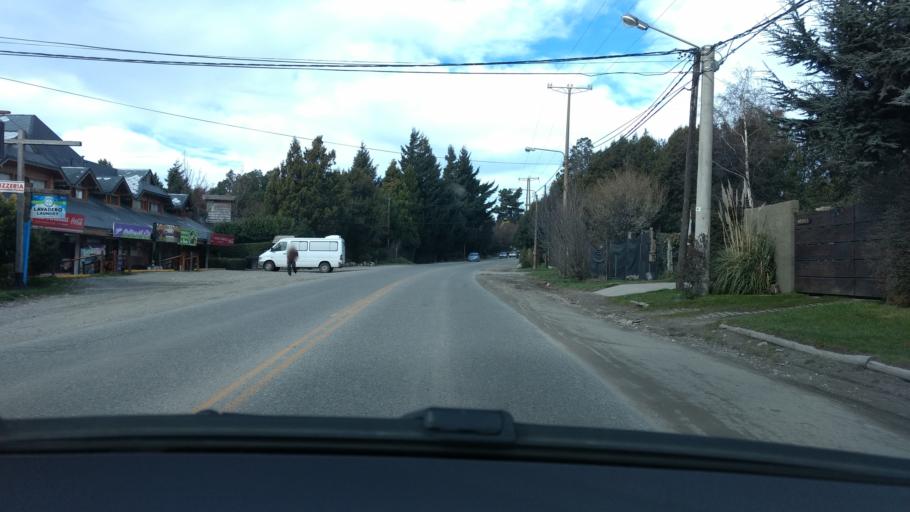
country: AR
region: Rio Negro
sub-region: Departamento de Bariloche
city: San Carlos de Bariloche
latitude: -41.1198
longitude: -71.3821
